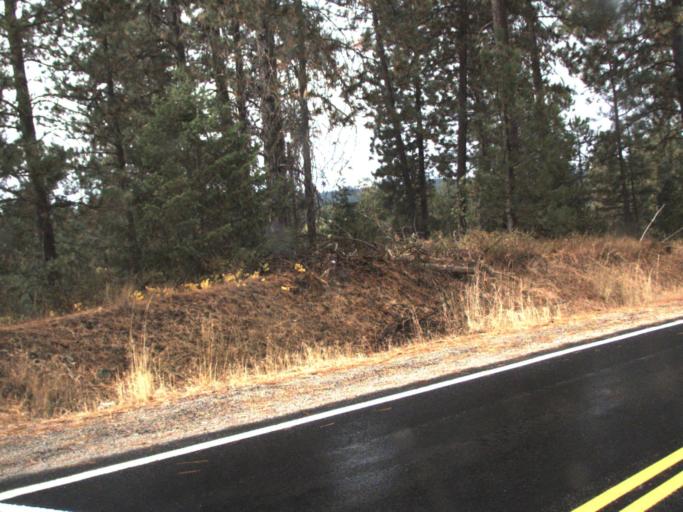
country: US
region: Washington
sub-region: Stevens County
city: Chewelah
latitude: 48.0633
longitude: -117.7620
